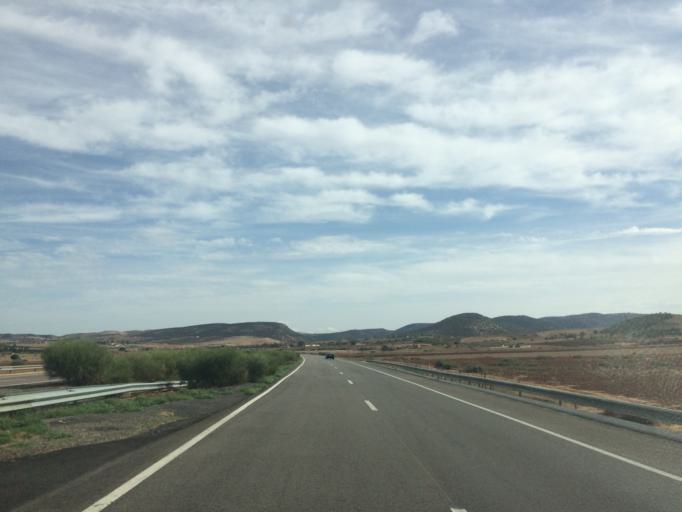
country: MA
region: Rabat-Sale-Zemmour-Zaer
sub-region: Khemisset
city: Khemisset
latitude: 33.7839
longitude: -5.9098
